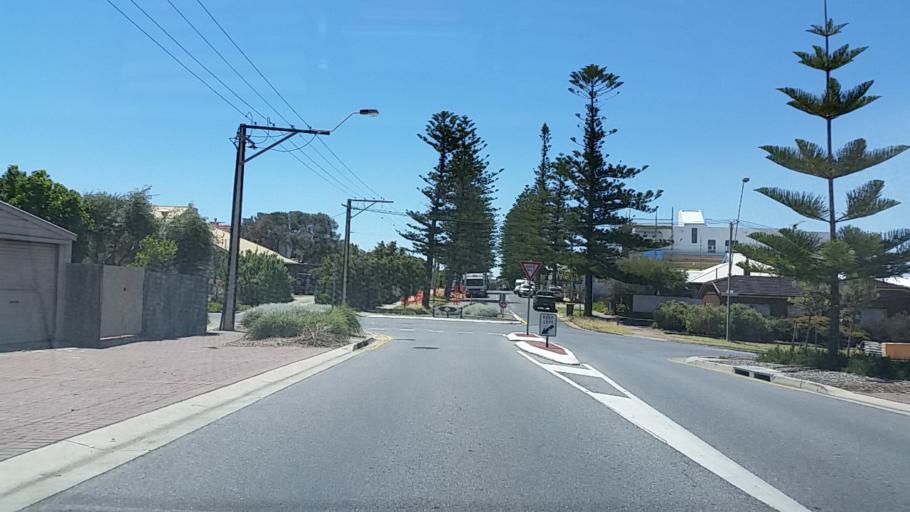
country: AU
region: South Australia
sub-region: Charles Sturt
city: Grange
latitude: -34.9001
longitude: 138.4895
